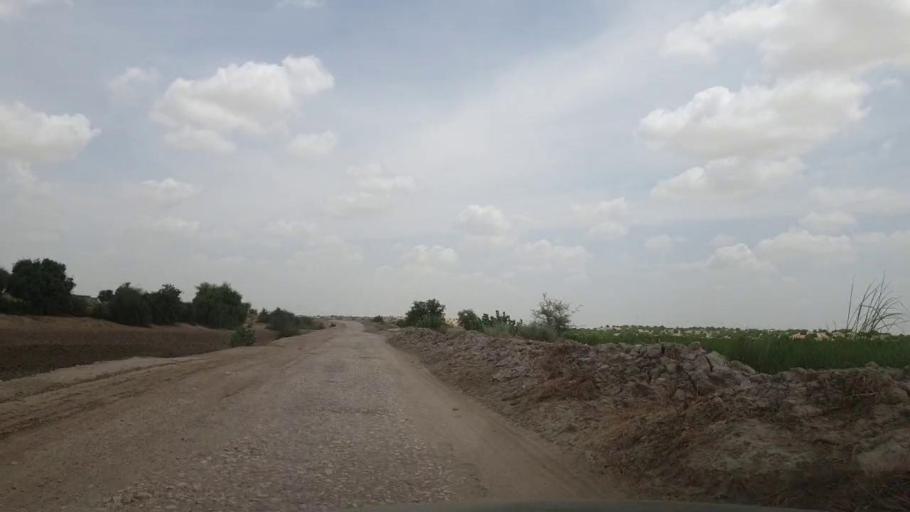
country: PK
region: Sindh
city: Kot Diji
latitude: 27.2022
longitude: 69.1219
